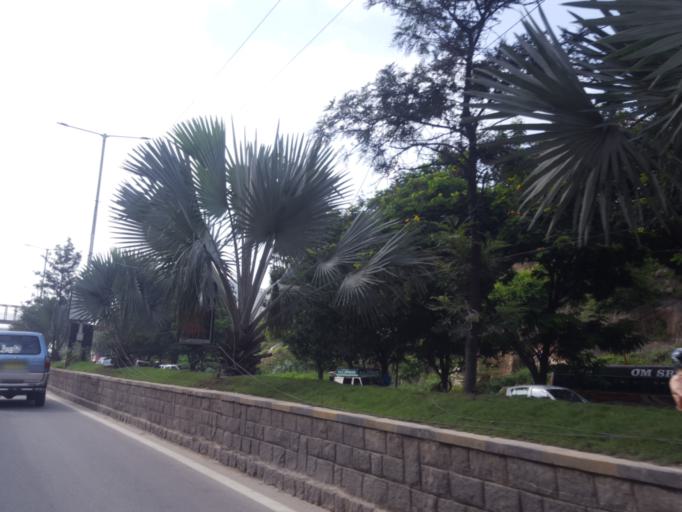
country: IN
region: Telangana
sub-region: Rangareddi
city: Kukatpalli
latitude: 17.4240
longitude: 78.3801
